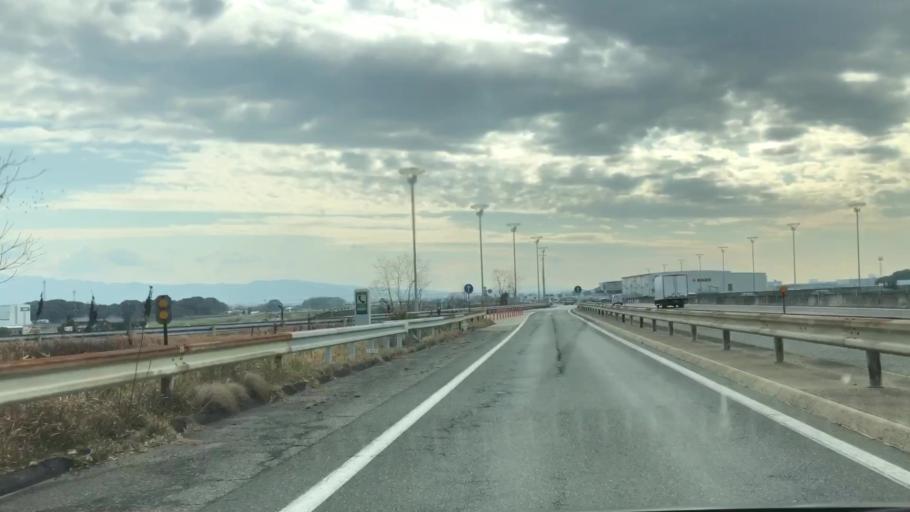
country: JP
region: Saga Prefecture
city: Tosu
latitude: 33.3953
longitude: 130.5386
